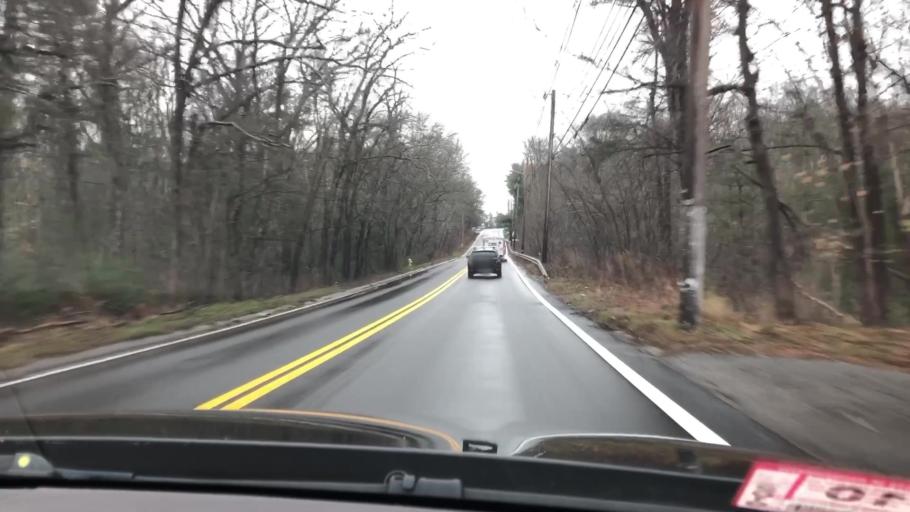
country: US
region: Massachusetts
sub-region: Norfolk County
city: Wrentham
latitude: 42.0818
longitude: -71.3094
